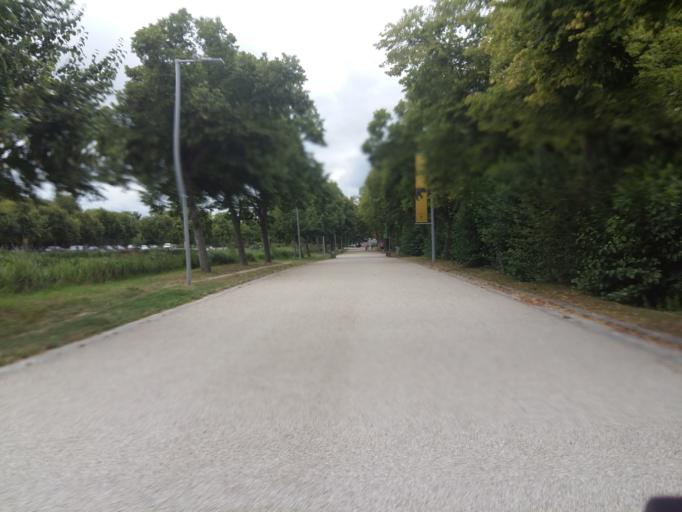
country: FR
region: Picardie
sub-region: Departement de la Somme
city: Amiens
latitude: 49.8997
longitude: 2.2769
